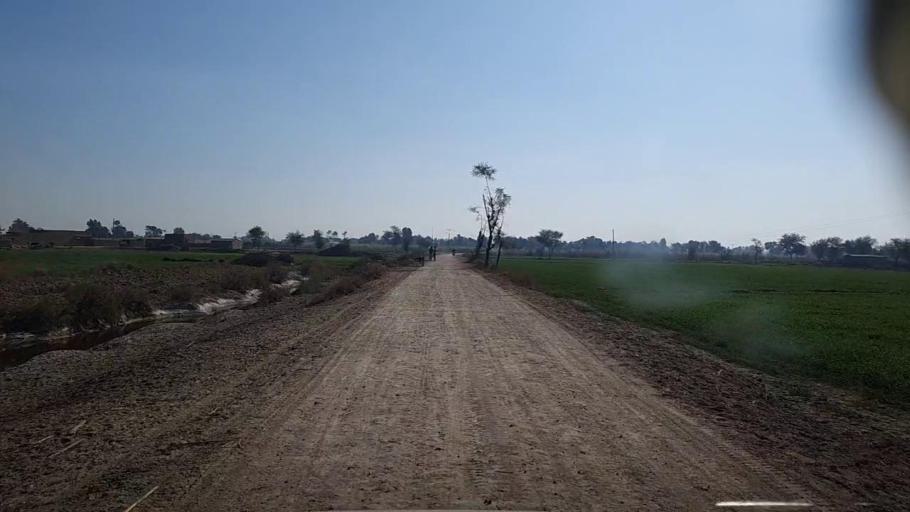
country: PK
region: Sindh
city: Khairpur
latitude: 28.0604
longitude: 69.7435
